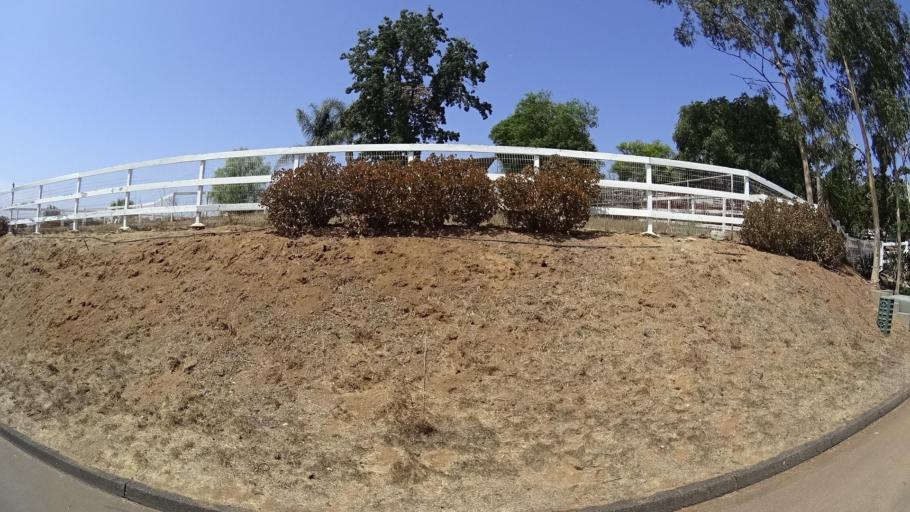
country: US
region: California
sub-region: San Diego County
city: Fallbrook
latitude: 33.3624
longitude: -117.2399
